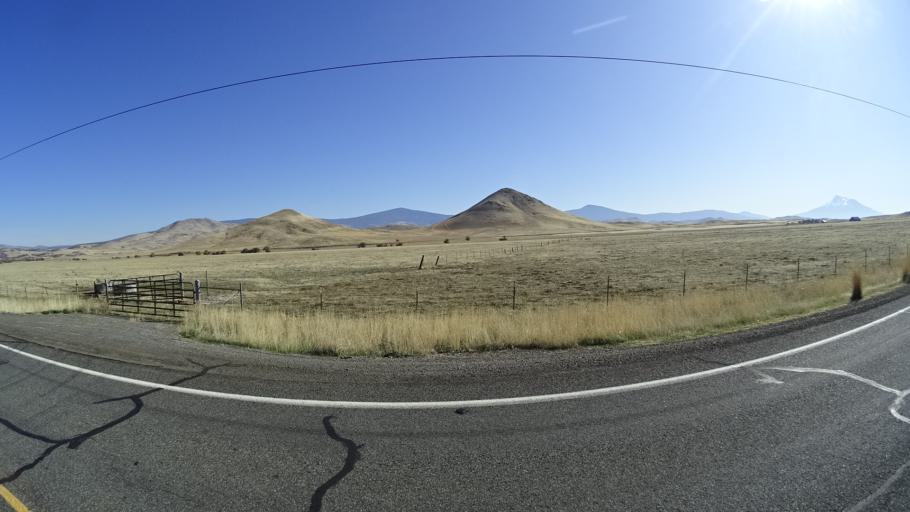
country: US
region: California
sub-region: Siskiyou County
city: Montague
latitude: 41.8249
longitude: -122.4955
